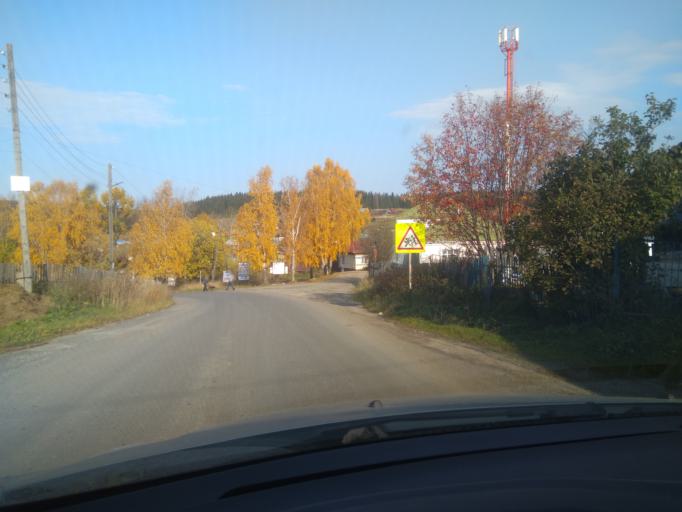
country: RU
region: Sverdlovsk
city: Nizhniye Sergi
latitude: 56.6764
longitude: 59.3353
